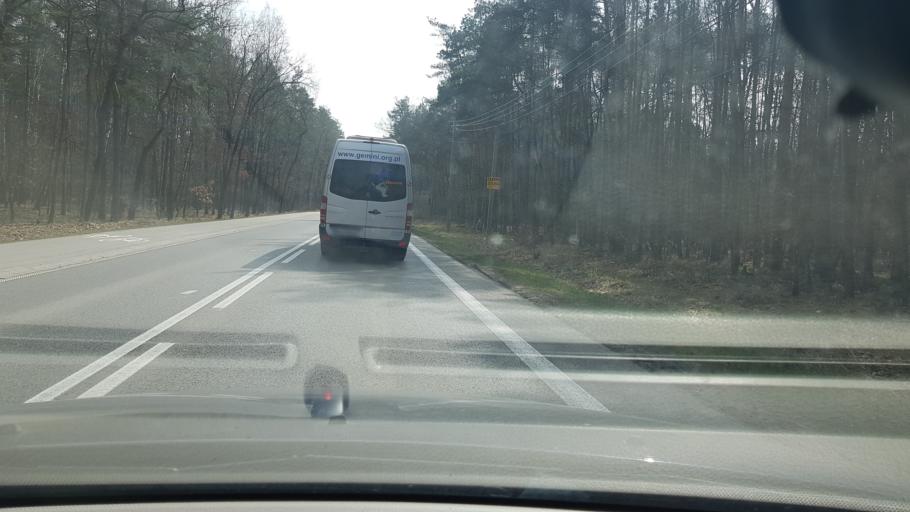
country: PL
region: Masovian Voivodeship
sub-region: Warszawa
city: Wesola
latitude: 52.2359
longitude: 21.2224
